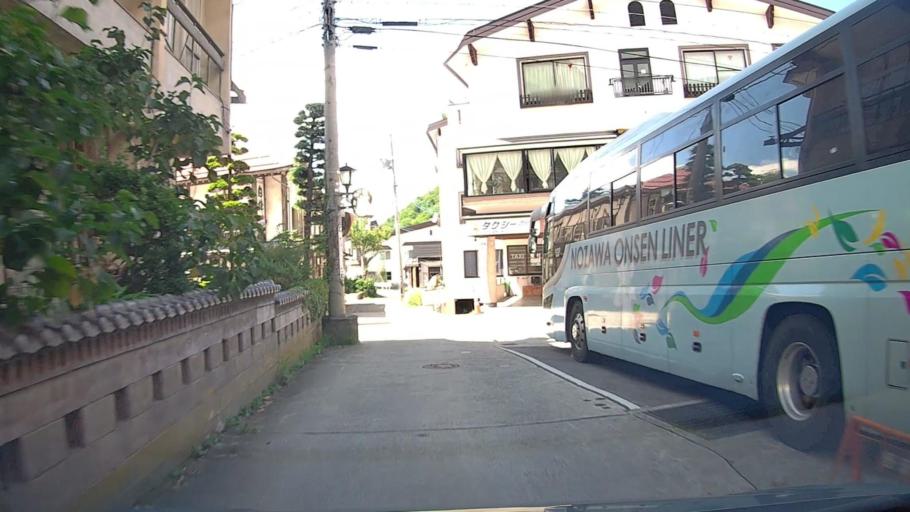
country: JP
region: Nagano
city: Iiyama
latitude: 36.9231
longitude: 138.4467
